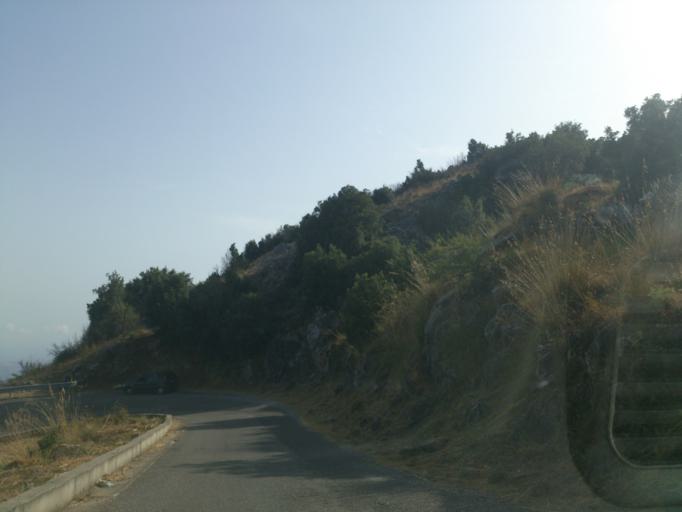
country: IT
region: Calabria
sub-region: Provincia di Reggio Calabria
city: Pazzano
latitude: 38.4658
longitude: 16.4407
